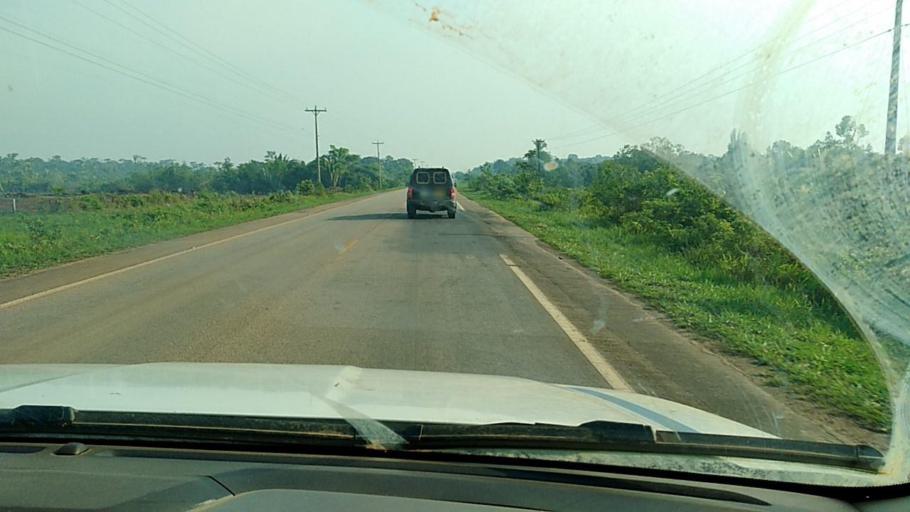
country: BR
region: Rondonia
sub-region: Porto Velho
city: Porto Velho
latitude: -8.3994
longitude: -63.9633
